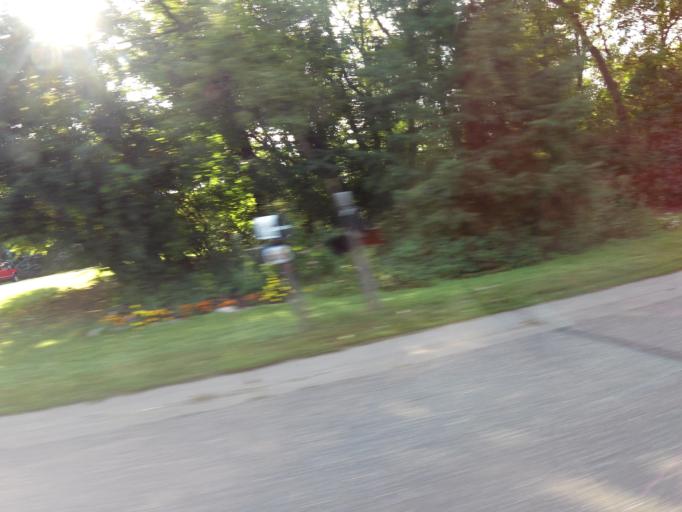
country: US
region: Minnesota
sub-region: Washington County
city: Oak Park Heights
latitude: 45.0209
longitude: -92.8071
